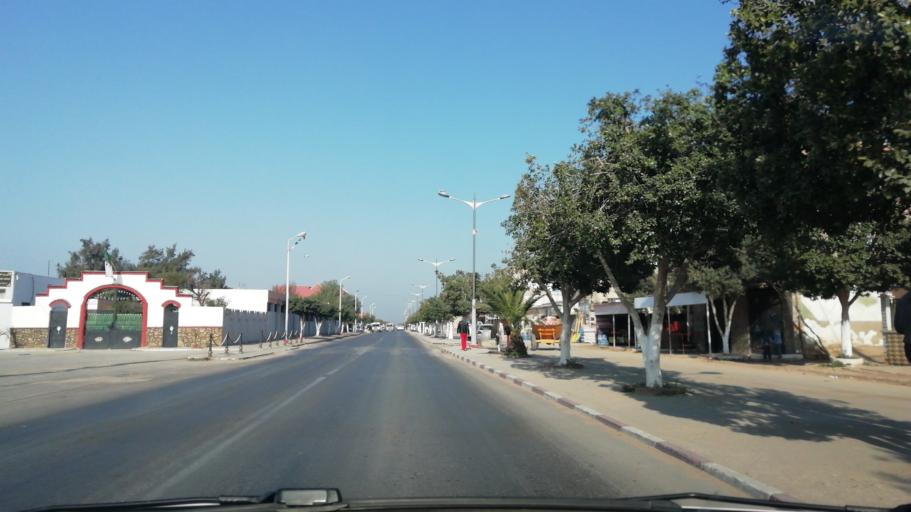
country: DZ
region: Mostaganem
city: Mostaganem
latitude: 35.7526
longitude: 0.1196
